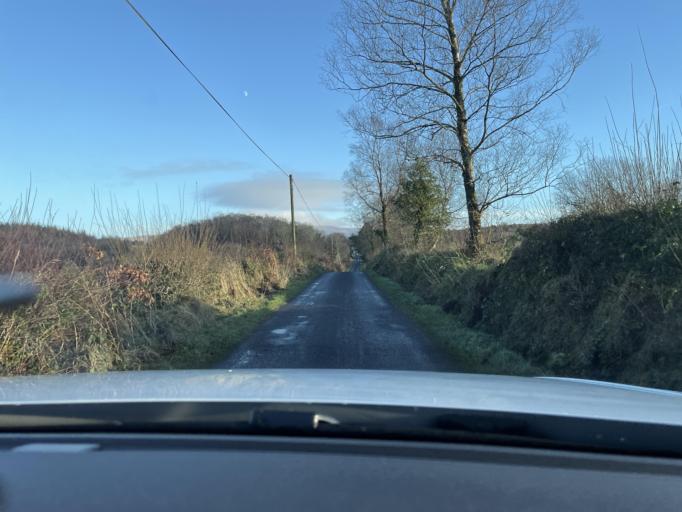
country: IE
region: Connaught
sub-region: County Leitrim
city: Manorhamilton
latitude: 54.2159
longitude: -7.9749
